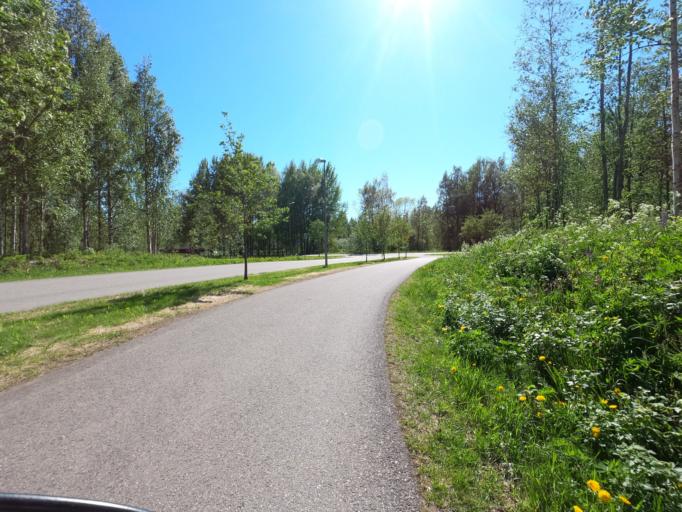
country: FI
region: North Karelia
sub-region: Joensuu
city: Joensuu
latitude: 62.6022
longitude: 29.8255
